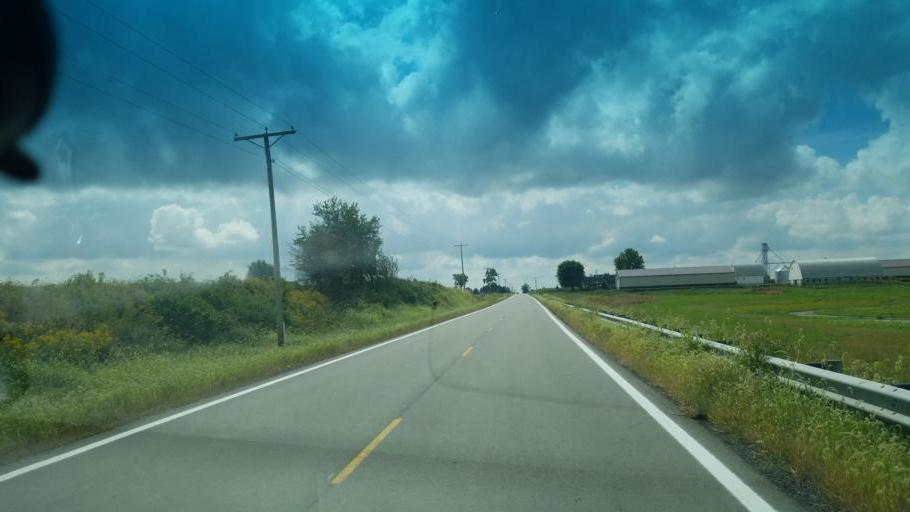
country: US
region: Ohio
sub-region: Crawford County
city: Bucyrus
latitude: 40.9853
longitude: -83.0164
